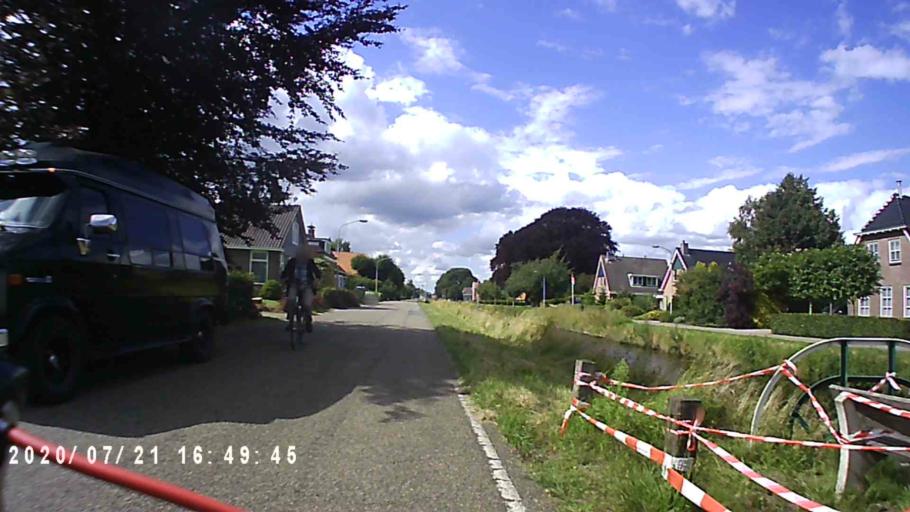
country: NL
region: Groningen
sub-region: Gemeente Hoogezand-Sappemeer
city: Hoogezand
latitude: 53.1206
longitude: 6.7732
